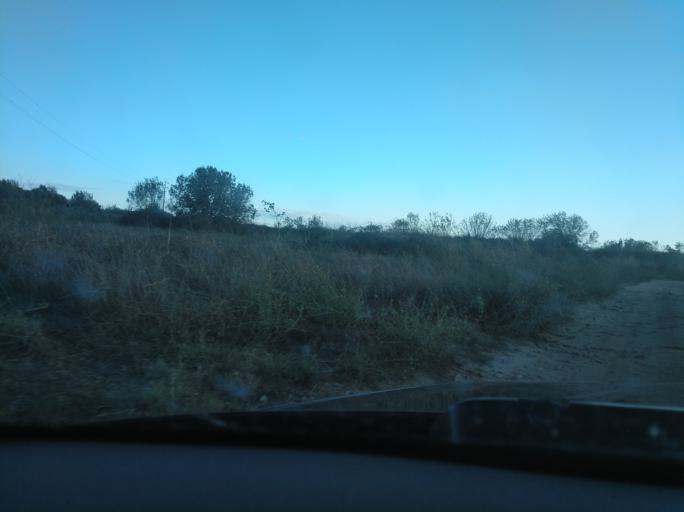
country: PT
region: Portalegre
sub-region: Campo Maior
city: Campo Maior
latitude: 39.0412
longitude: -6.9775
